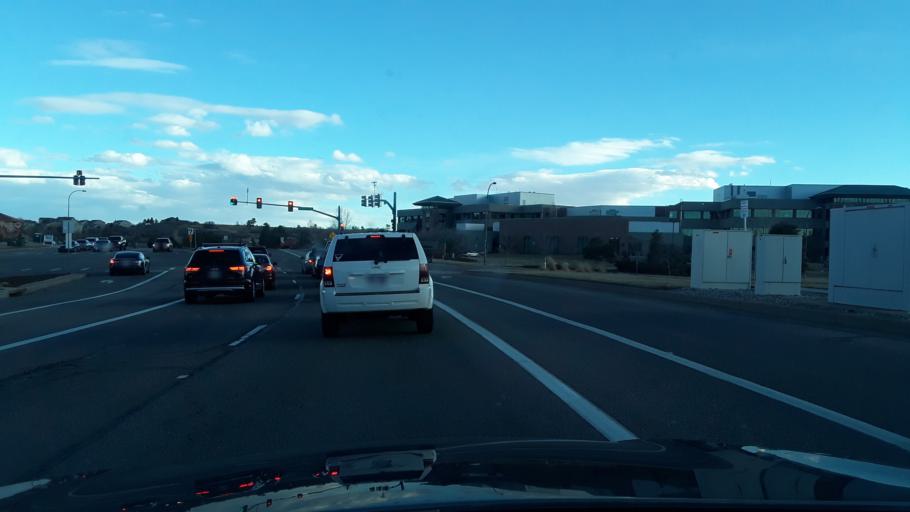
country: US
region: Colorado
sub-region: El Paso County
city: Gleneagle
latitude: 39.0111
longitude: -104.8088
